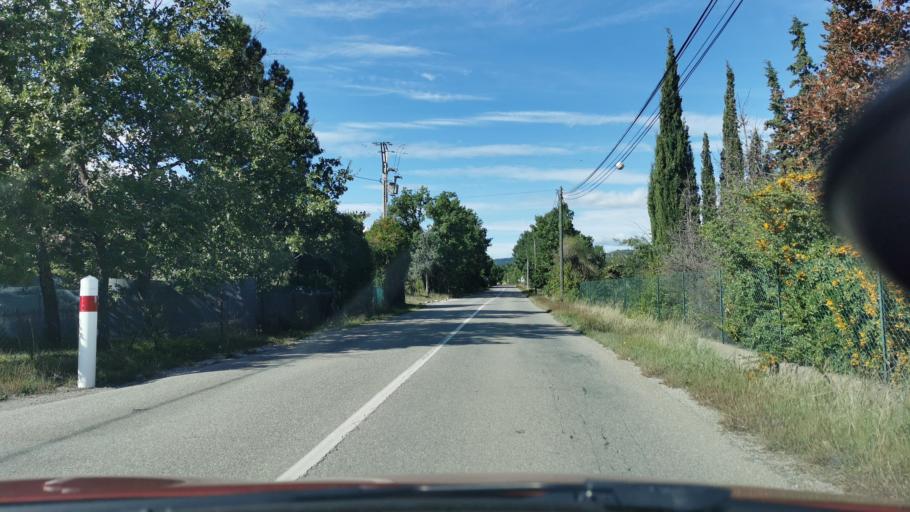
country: FR
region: Provence-Alpes-Cote d'Azur
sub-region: Departement des Alpes-de-Haute-Provence
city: Peipin
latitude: 44.1533
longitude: 5.9749
